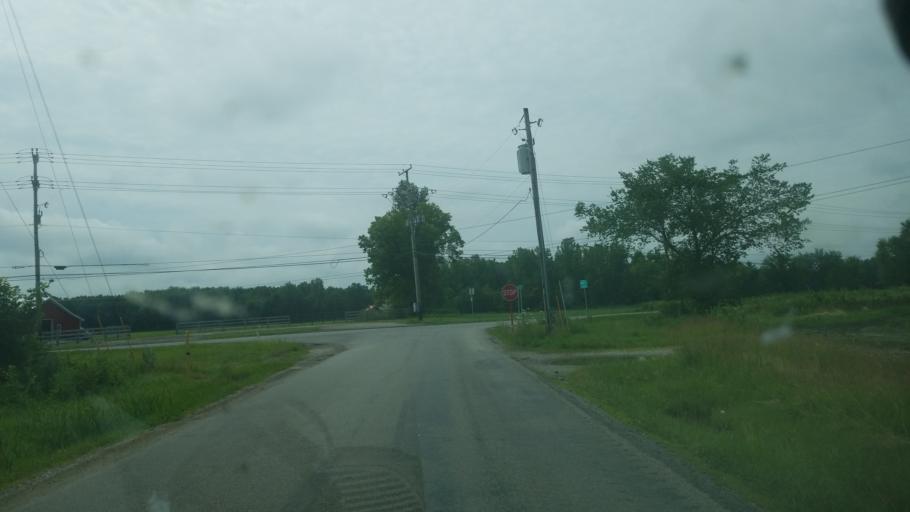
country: US
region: Ohio
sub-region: Franklin County
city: New Albany
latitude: 40.1213
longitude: -82.7622
